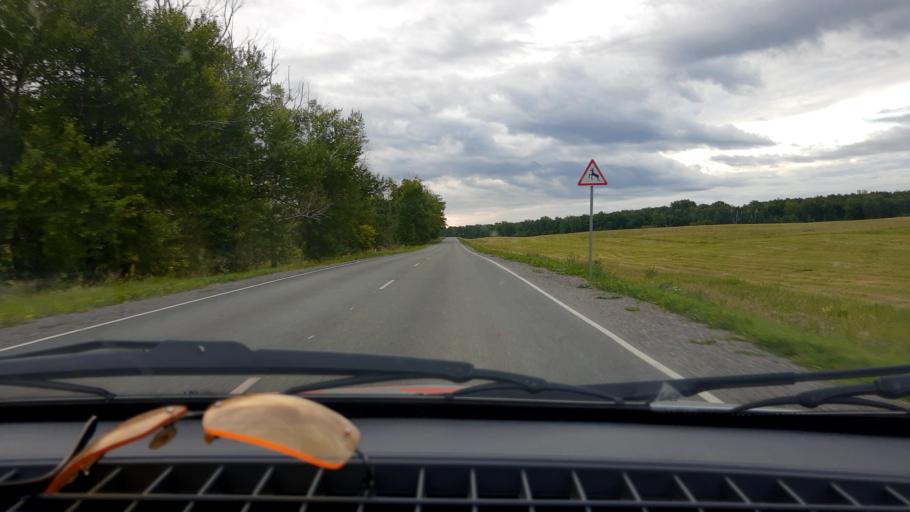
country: RU
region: Bashkortostan
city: Chishmy
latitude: 54.5631
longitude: 55.4908
